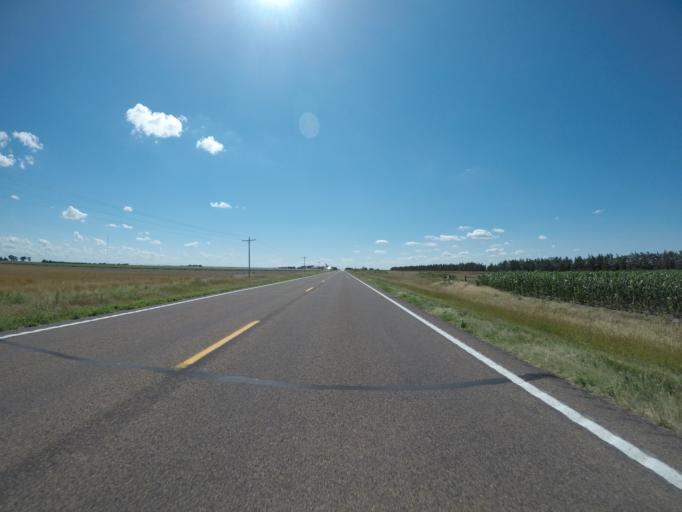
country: US
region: Nebraska
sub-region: Chase County
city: Imperial
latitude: 40.5376
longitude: -101.6568
